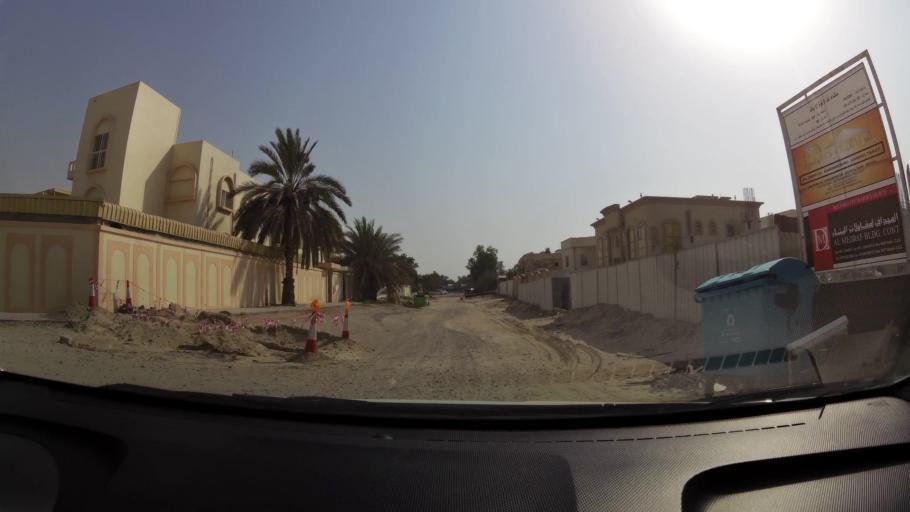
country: AE
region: Ajman
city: Ajman
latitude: 25.3873
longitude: 55.4288
